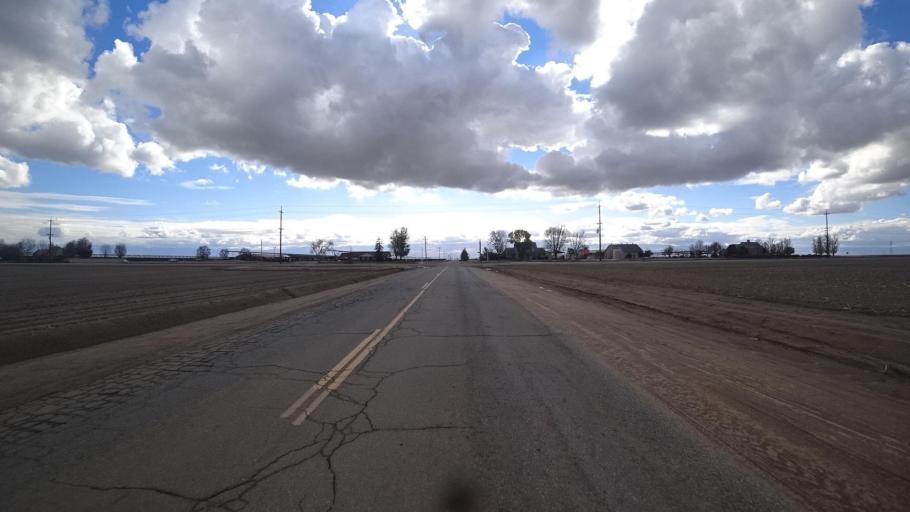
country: US
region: California
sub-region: Kern County
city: Greenfield
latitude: 35.2097
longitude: -119.0569
